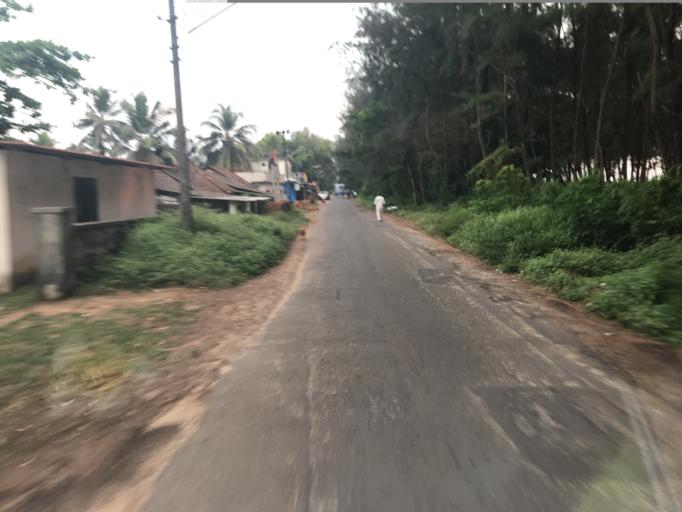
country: IN
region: Karnataka
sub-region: Dakshina Kannada
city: Mangalore
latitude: 12.8888
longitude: 74.8159
